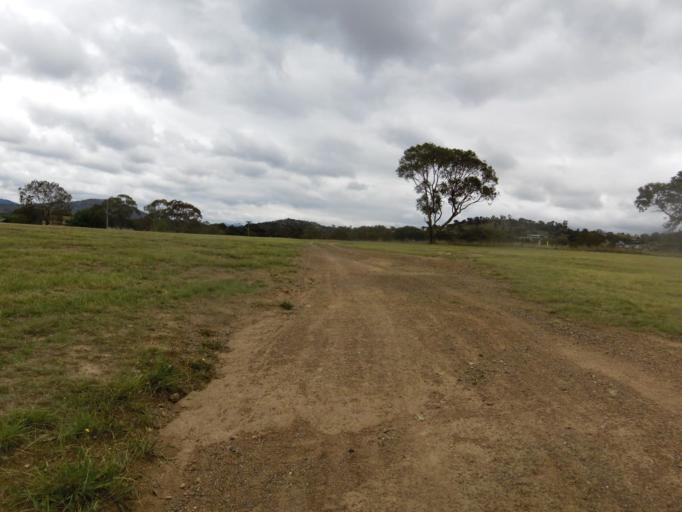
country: AU
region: Australian Capital Territory
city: Macquarie
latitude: -35.3447
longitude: 149.0273
